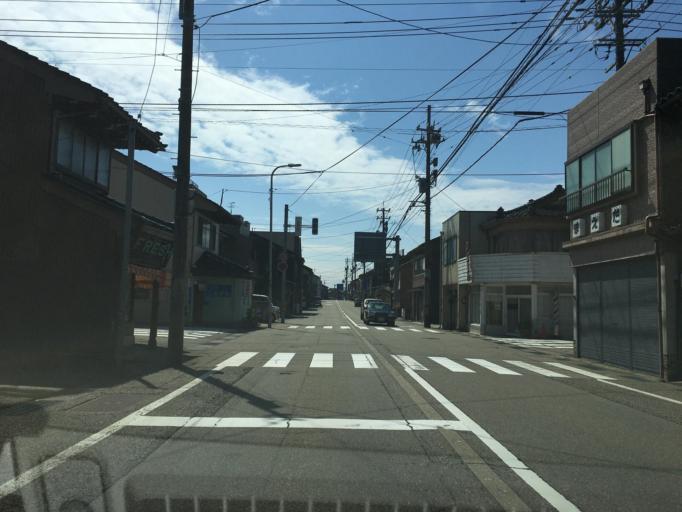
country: JP
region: Toyama
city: Himi
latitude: 36.8489
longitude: 136.9876
